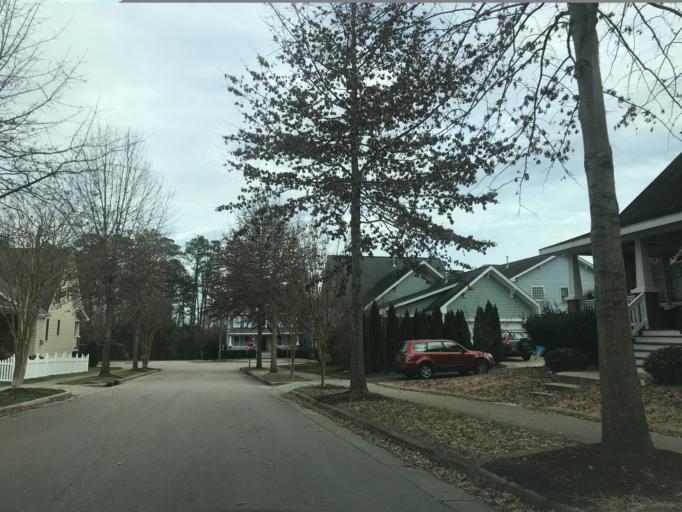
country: US
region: North Carolina
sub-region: Wake County
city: Wake Forest
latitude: 35.9249
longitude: -78.5681
